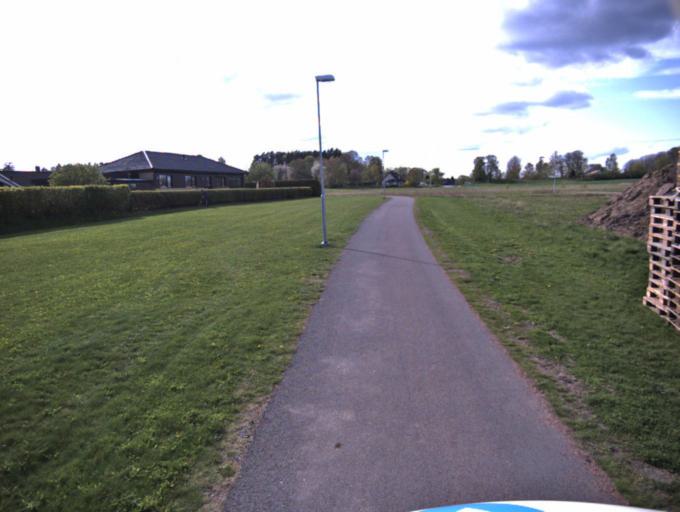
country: SE
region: Skane
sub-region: Kristianstads Kommun
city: Norra Asum
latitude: 56.0080
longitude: 14.0839
